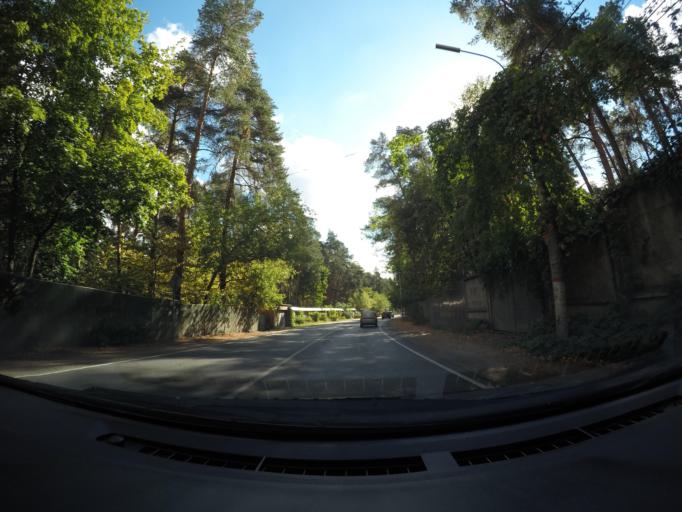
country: RU
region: Moskovskaya
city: Zhukovskiy
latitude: 55.6054
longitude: 38.1461
